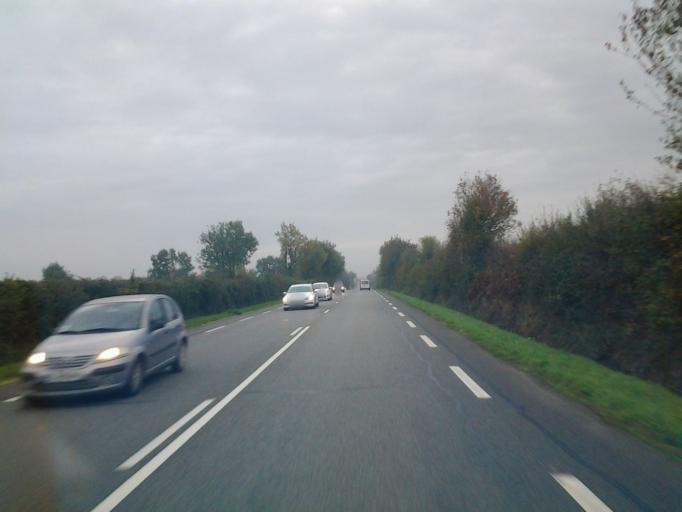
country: FR
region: Pays de la Loire
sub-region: Departement de la Vendee
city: Saint-Florent-des-Bois
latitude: 46.6042
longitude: -1.3346
